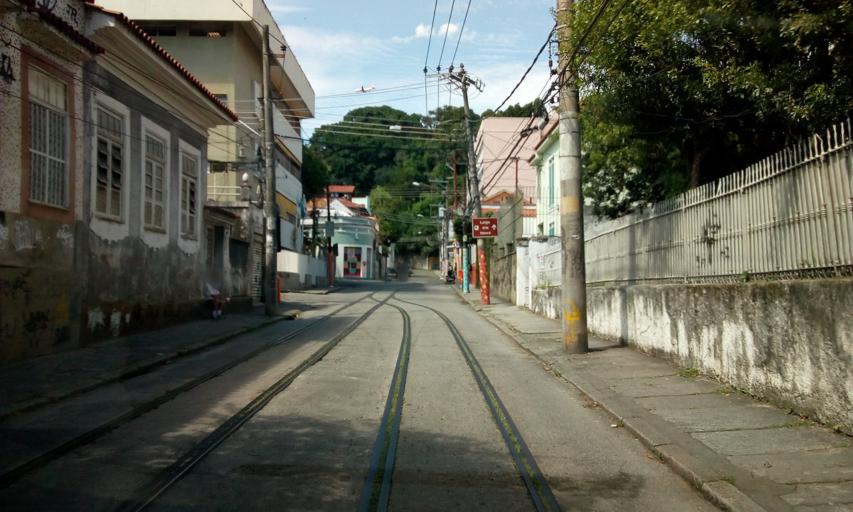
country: BR
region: Rio de Janeiro
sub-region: Rio De Janeiro
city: Rio de Janeiro
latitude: -22.9209
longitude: -43.1890
